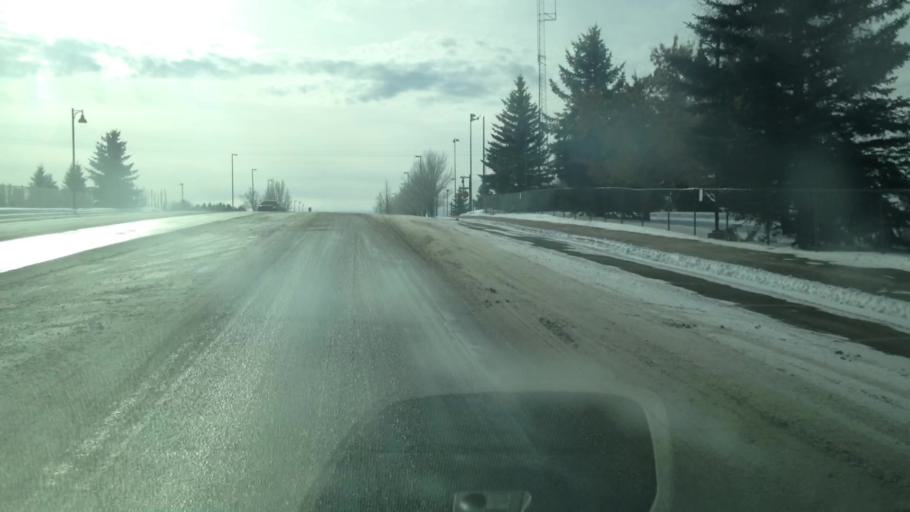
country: US
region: Idaho
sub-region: Madison County
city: Rexburg
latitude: 43.8126
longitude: -111.7838
